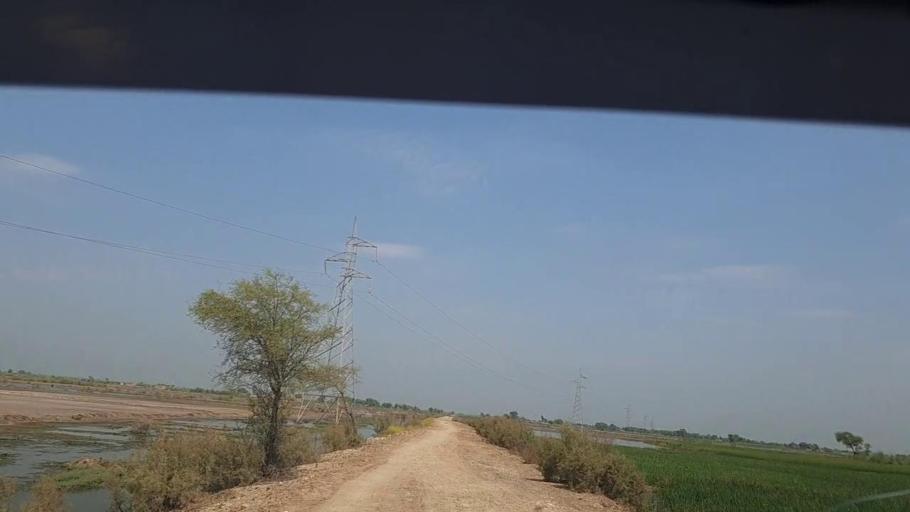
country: PK
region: Sindh
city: Thul
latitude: 28.2218
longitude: 68.6767
